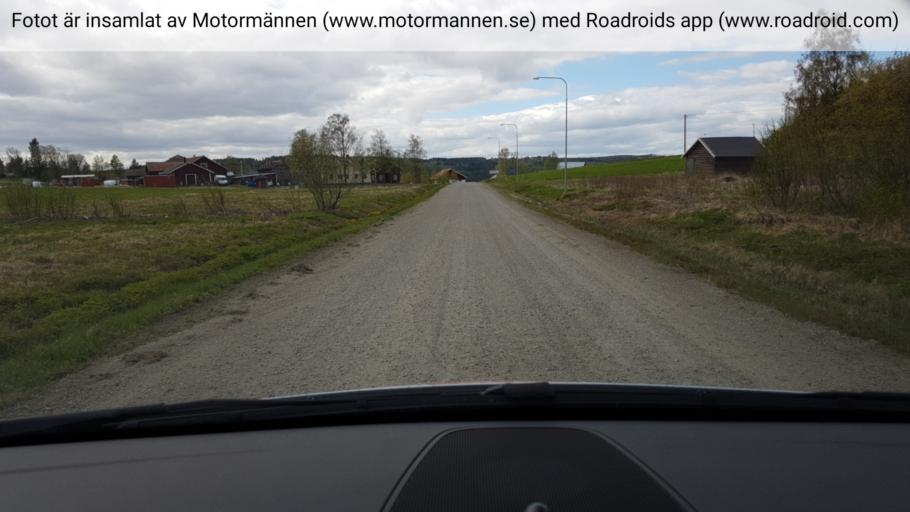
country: SE
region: Jaemtland
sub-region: OEstersunds Kommun
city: Brunflo
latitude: 62.9539
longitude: 14.9202
